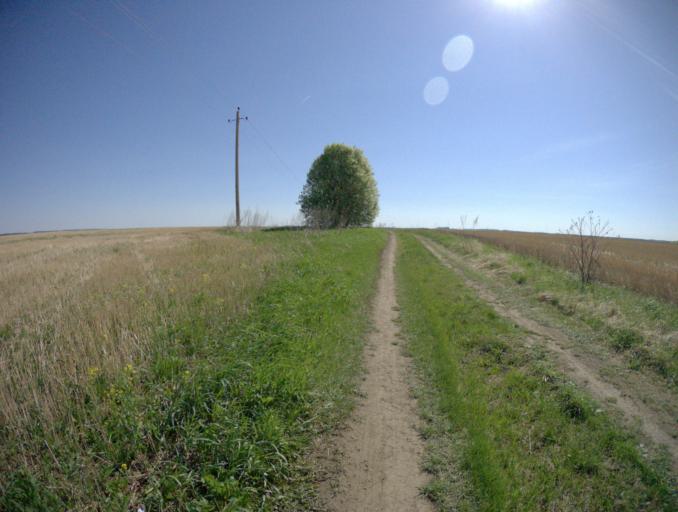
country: RU
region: Vladimir
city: Vladimir
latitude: 56.2623
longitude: 40.3132
